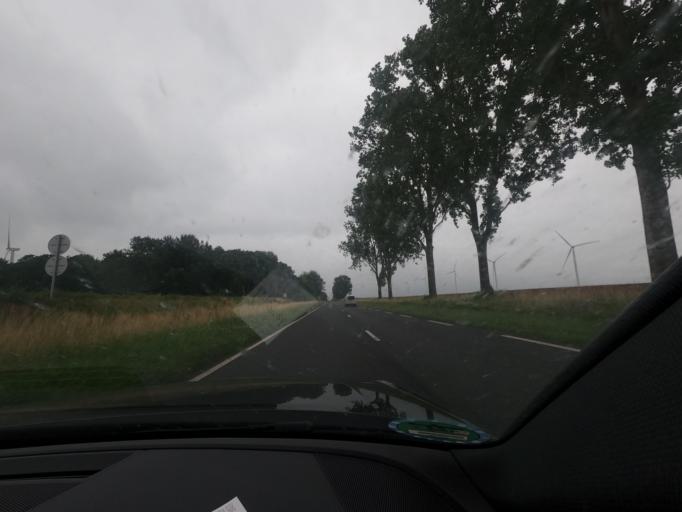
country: FR
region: Picardie
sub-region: Departement de la Somme
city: Roye
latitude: 49.7213
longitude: 2.7344
